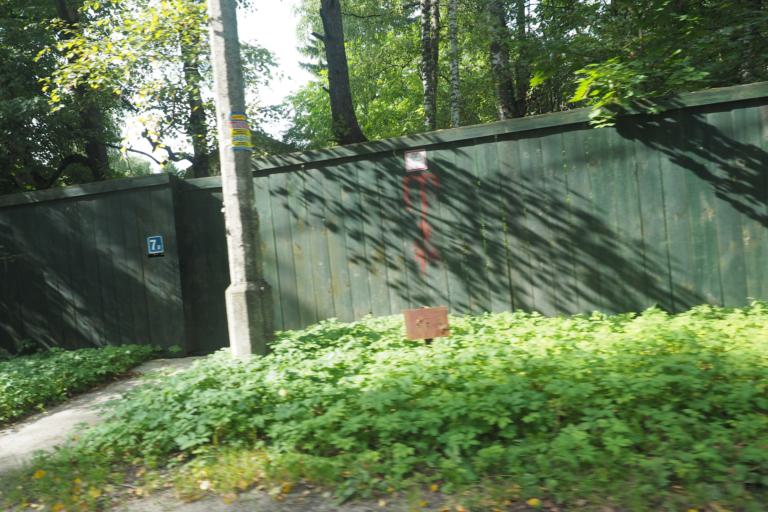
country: RU
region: Moskovskaya
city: Kratovo
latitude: 55.5907
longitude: 38.1950
